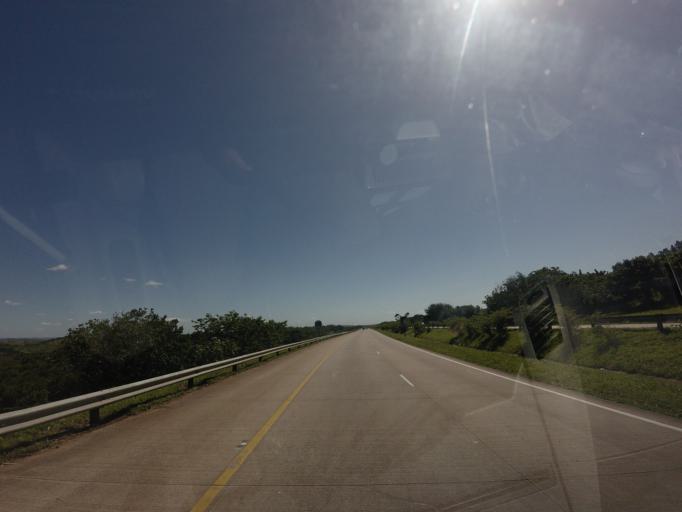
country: ZA
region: KwaZulu-Natal
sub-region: iLembe District Municipality
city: Ballitoville
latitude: -29.4719
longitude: 31.2336
